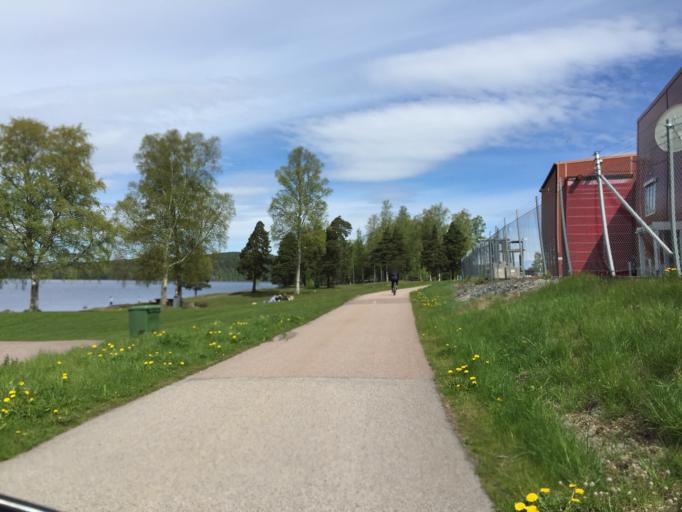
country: SE
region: Dalarna
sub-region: Ludvika Kommun
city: Ludvika
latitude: 60.1462
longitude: 15.1672
